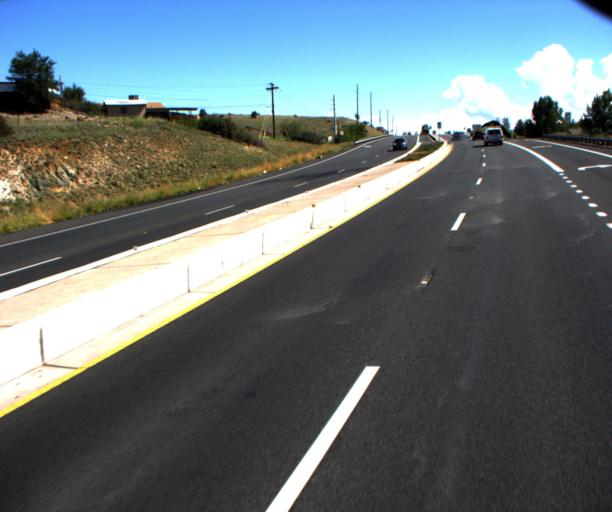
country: US
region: Arizona
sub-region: Yavapai County
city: Prescott Valley
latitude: 34.5706
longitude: -112.3701
